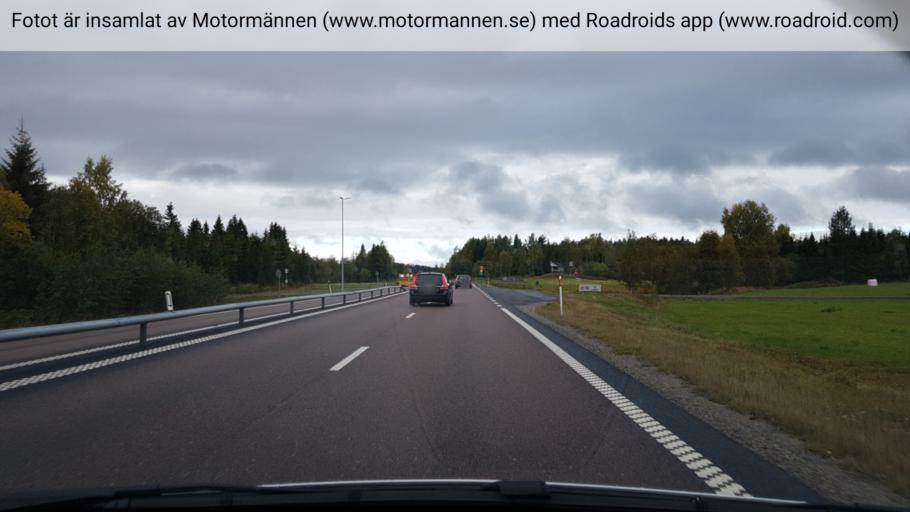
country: SE
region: Vaesternorrland
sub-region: OErnskoeldsviks Kommun
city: Ornskoldsvik
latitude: 63.3013
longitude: 18.8618
